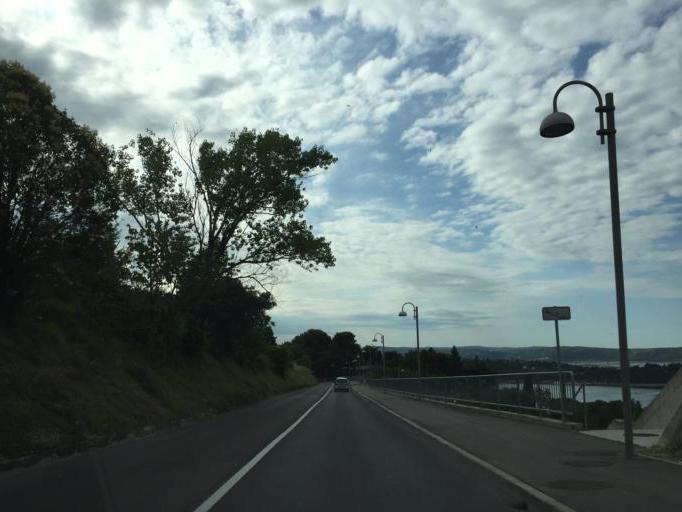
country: SI
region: Piran-Pirano
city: Portoroz
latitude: 45.5185
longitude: 13.5829
